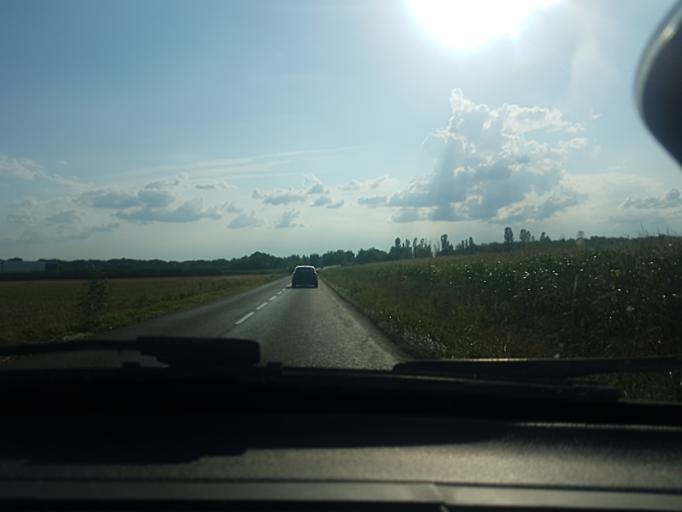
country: FR
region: Bourgogne
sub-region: Departement de Saone-et-Loire
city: Varennes-le-Grand
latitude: 46.7014
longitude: 4.8484
